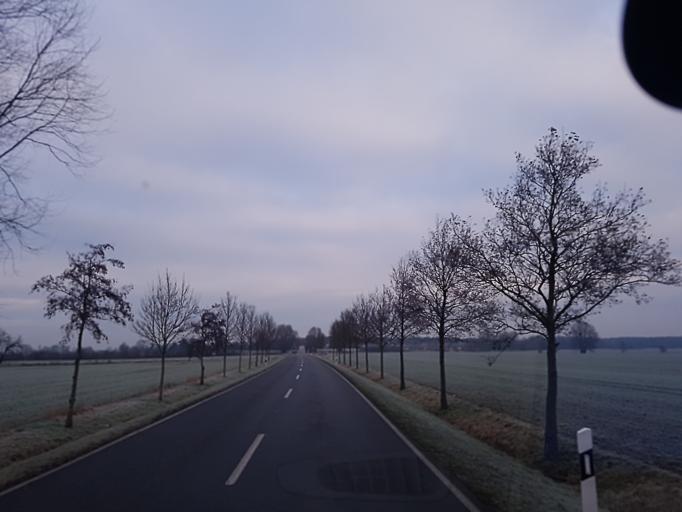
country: DE
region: Brandenburg
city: Finsterwalde
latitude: 51.6790
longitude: 13.7218
